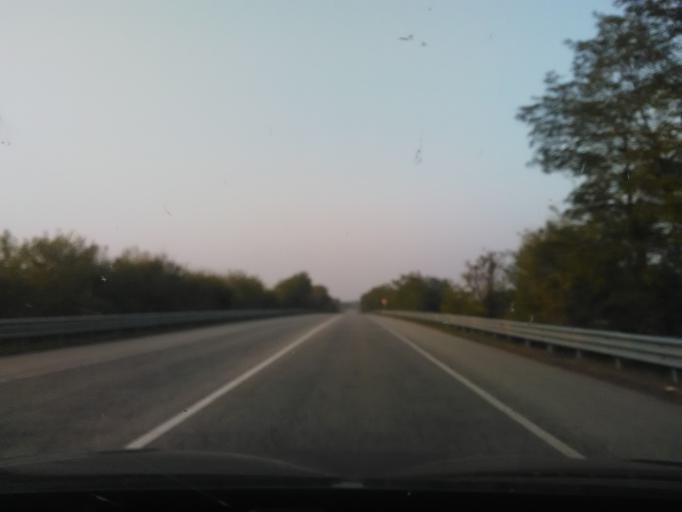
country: IT
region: Piedmont
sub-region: Provincia di Vercelli
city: Stroppiana
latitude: 45.2485
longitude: 8.4598
